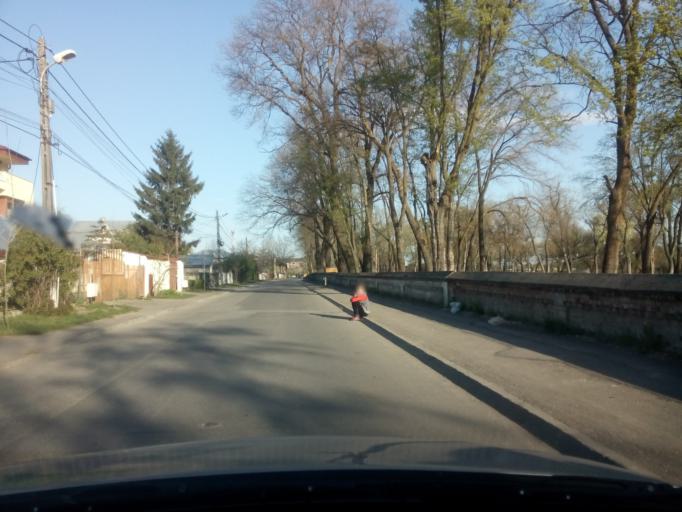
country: RO
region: Ilfov
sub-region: Comuna Mogosoaia
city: Mogosoaia
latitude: 44.5255
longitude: 26.0012
